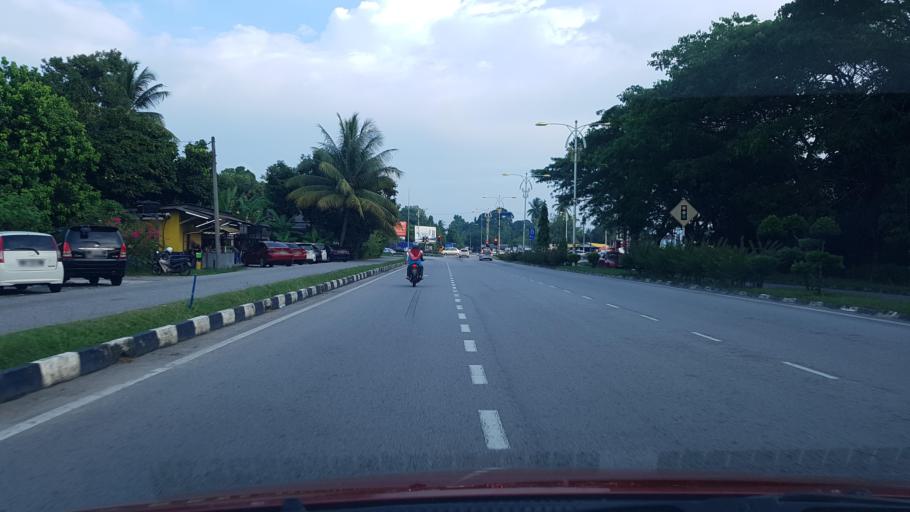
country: MY
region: Terengganu
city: Kuala Terengganu
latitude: 5.3409
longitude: 103.1021
